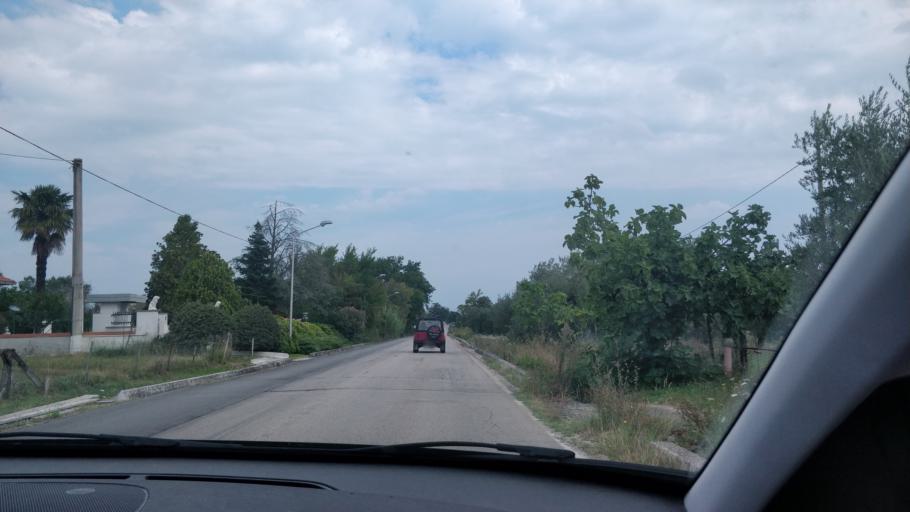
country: IT
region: Abruzzo
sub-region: Provincia di Chieti
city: San Vito Chietino
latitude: 42.2834
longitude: 14.4391
